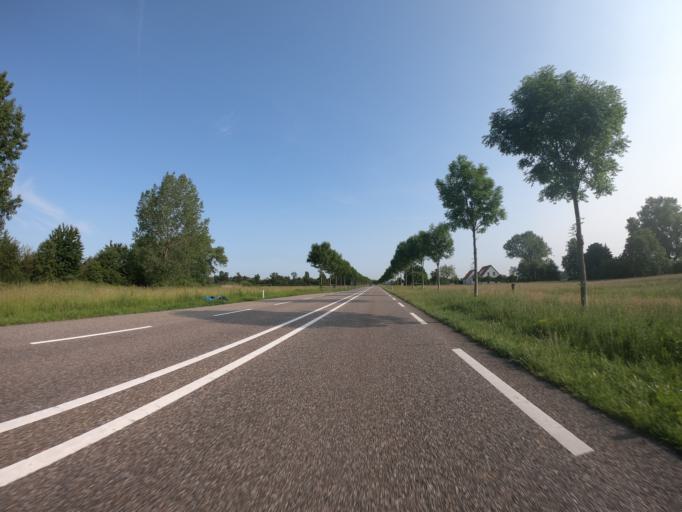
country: NL
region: North Brabant
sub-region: Gemeente Landerd
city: Reek
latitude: 51.7779
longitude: 5.6663
